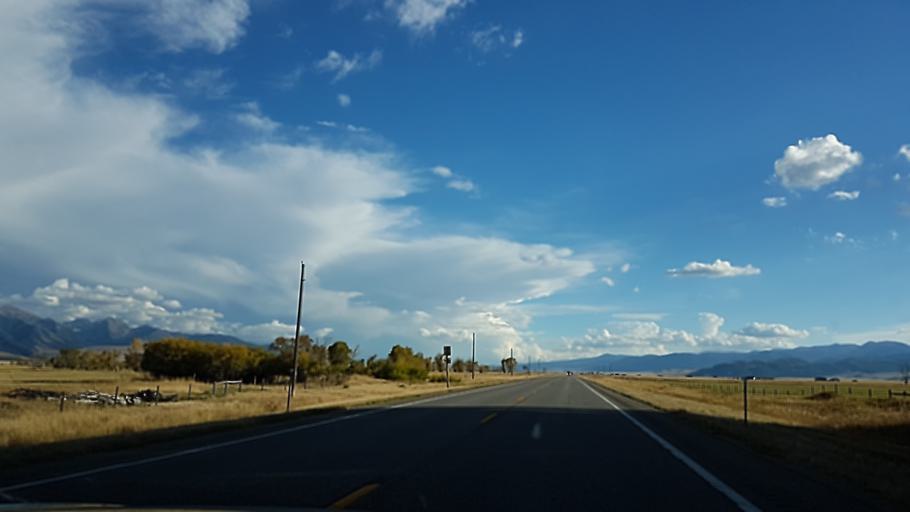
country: US
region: Montana
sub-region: Madison County
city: Virginia City
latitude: 45.2000
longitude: -111.6788
